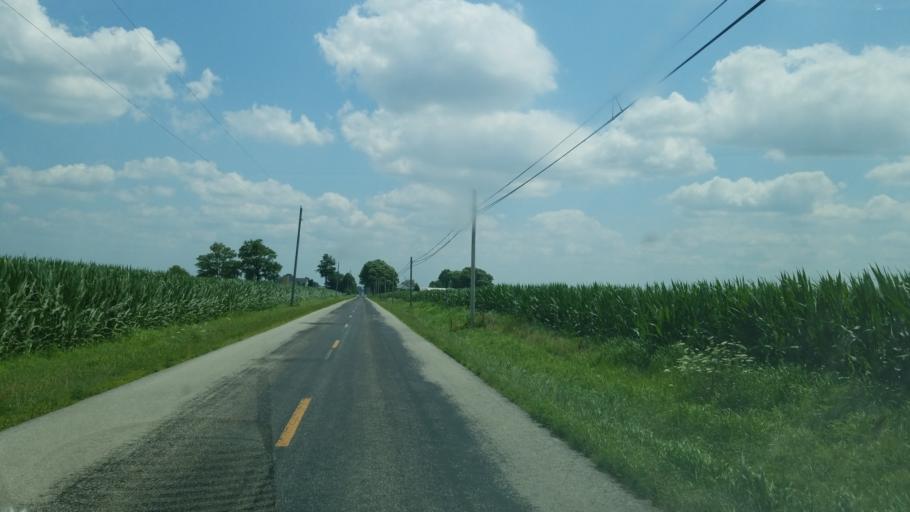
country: US
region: Ohio
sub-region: Henry County
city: Napoleon
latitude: 41.3414
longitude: -84.1122
